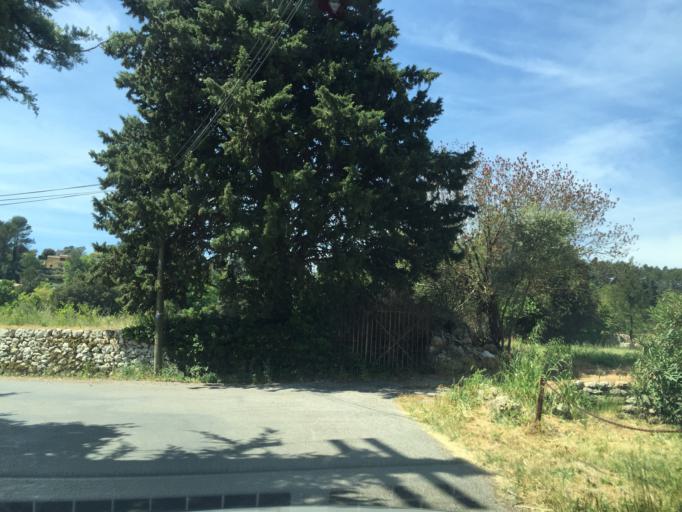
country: FR
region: Provence-Alpes-Cote d'Azur
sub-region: Departement du Var
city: Lorgues
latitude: 43.4861
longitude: 6.3633
